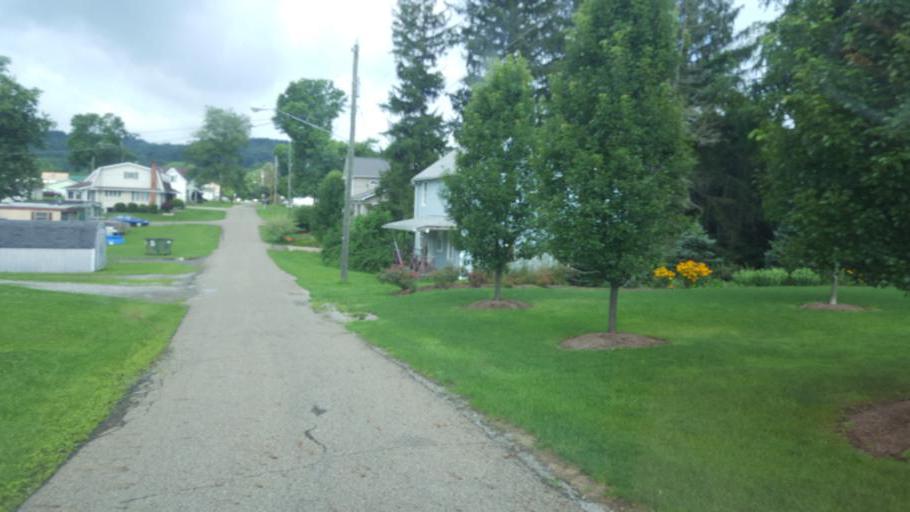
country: US
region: Ohio
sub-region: Columbiana County
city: Salineville
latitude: 40.5216
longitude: -80.8810
